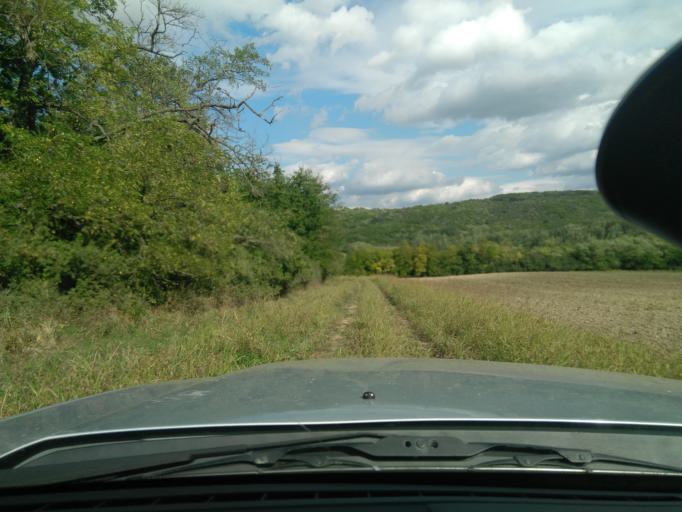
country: HU
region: Fejer
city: Bicske
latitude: 47.4642
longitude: 18.6735
